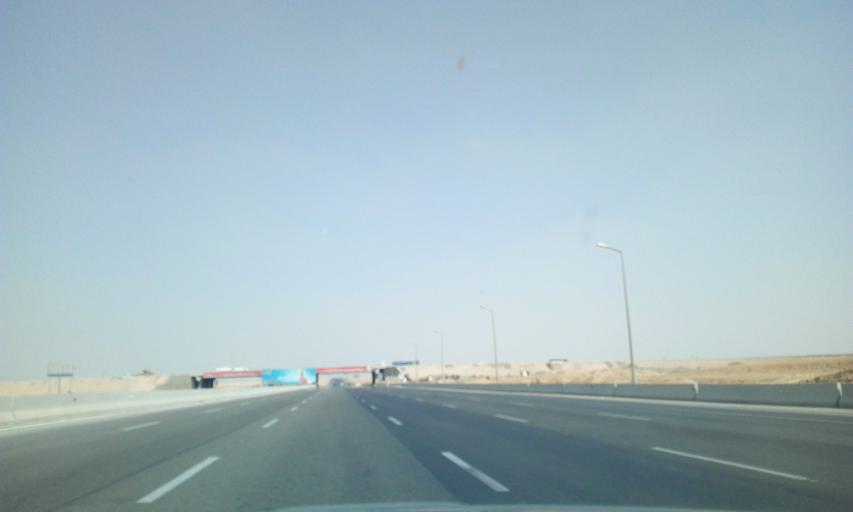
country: EG
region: Muhafazat al Qahirah
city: Halwan
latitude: 29.9061
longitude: 31.6900
